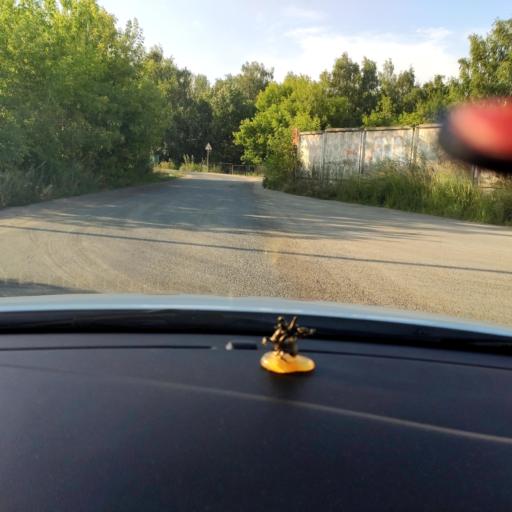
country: RU
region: Tatarstan
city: Staroye Arakchino
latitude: 55.8122
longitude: 48.9131
